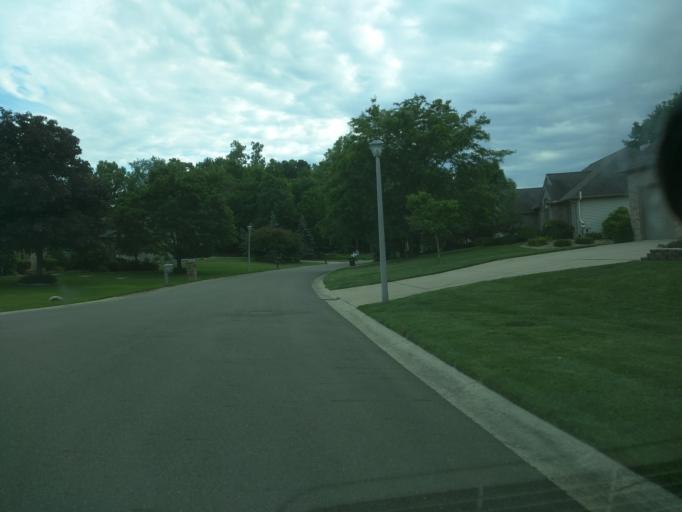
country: US
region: Michigan
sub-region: Eaton County
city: Waverly
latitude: 42.7531
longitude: -84.6154
